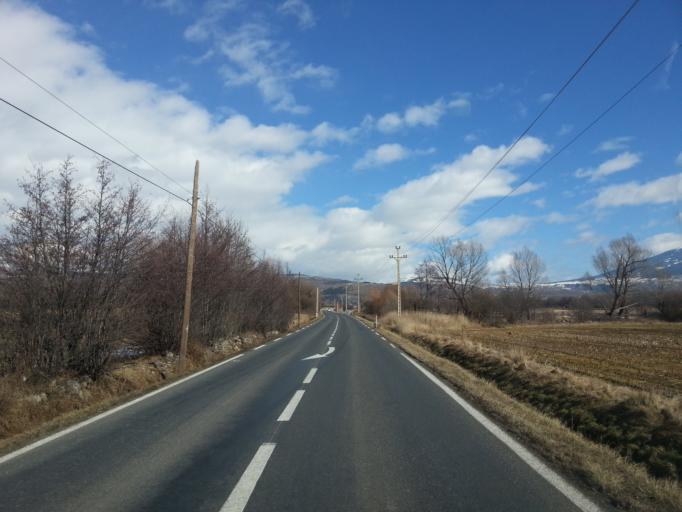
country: FR
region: Languedoc-Roussillon
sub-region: Departement des Pyrenees-Orientales
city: la Guingueta d'Ix
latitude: 42.4477
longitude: 1.9493
